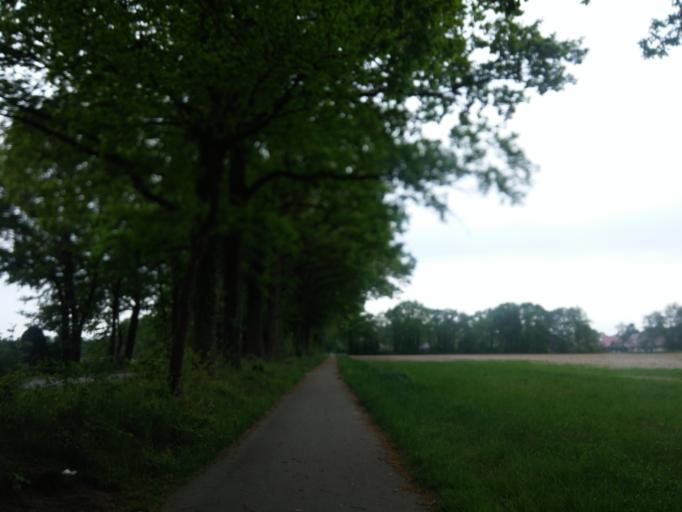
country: DE
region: Lower Saxony
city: Wietmarschen
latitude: 52.5071
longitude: 7.1389
